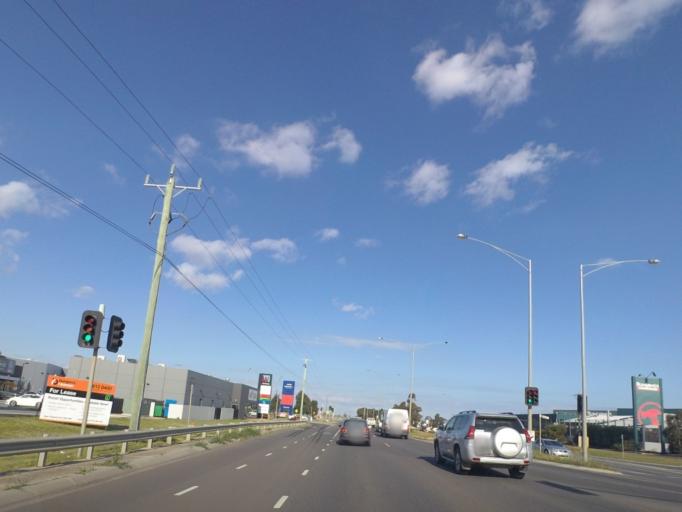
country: AU
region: Victoria
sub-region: Melton
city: Caroline Springs
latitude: -37.7587
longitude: 144.7472
